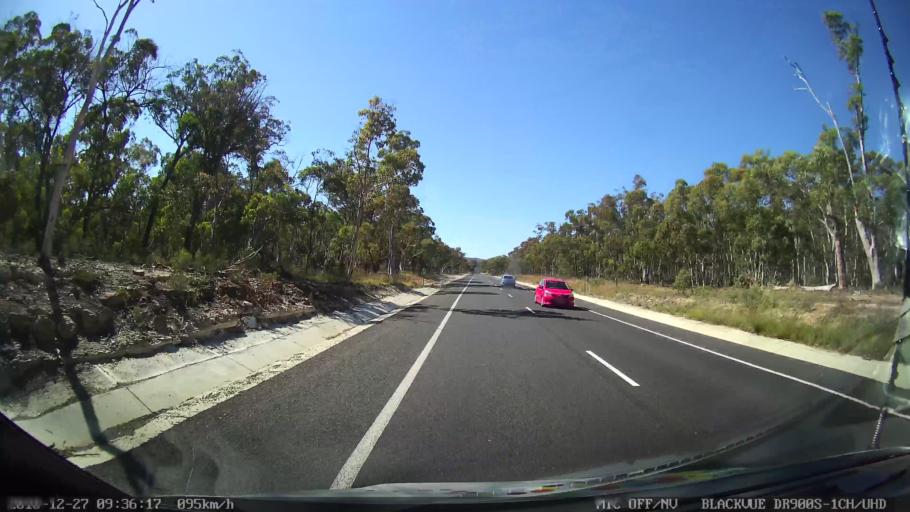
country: AU
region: New South Wales
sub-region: Lithgow
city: Portland
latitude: -33.2502
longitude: 150.0343
